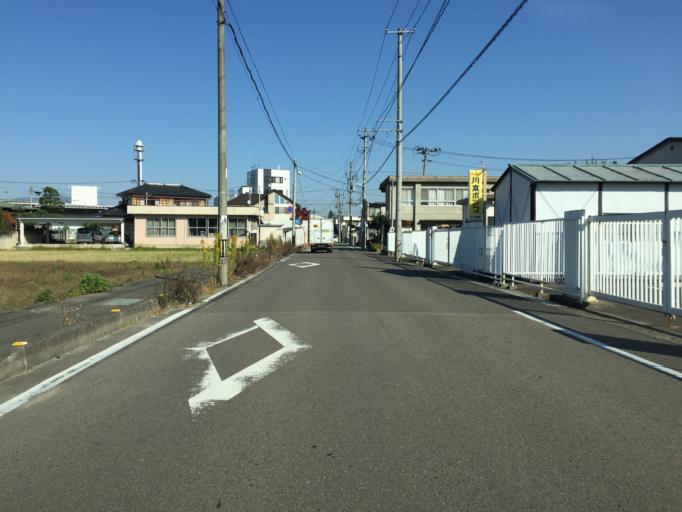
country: JP
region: Fukushima
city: Fukushima-shi
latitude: 37.7706
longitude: 140.4882
